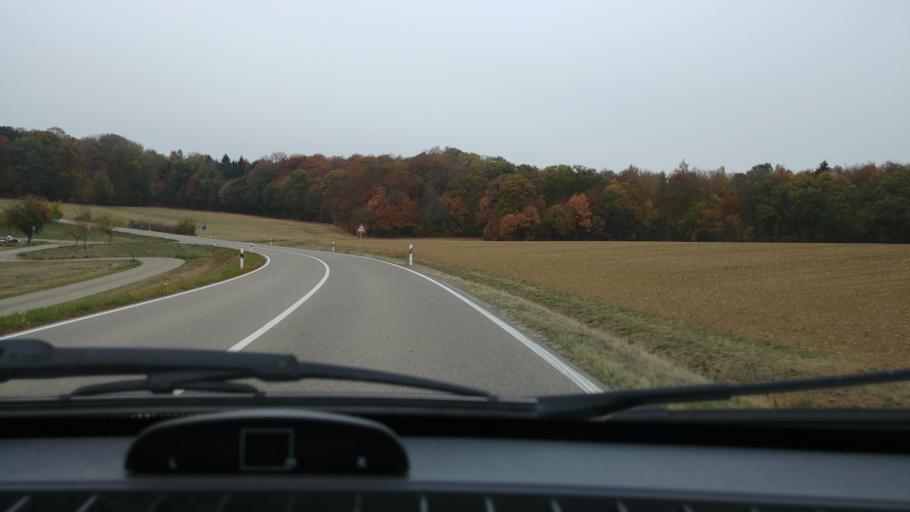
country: DE
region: Baden-Wuerttemberg
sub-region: Regierungsbezirk Stuttgart
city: Niederstetten
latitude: 49.3671
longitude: 9.8867
